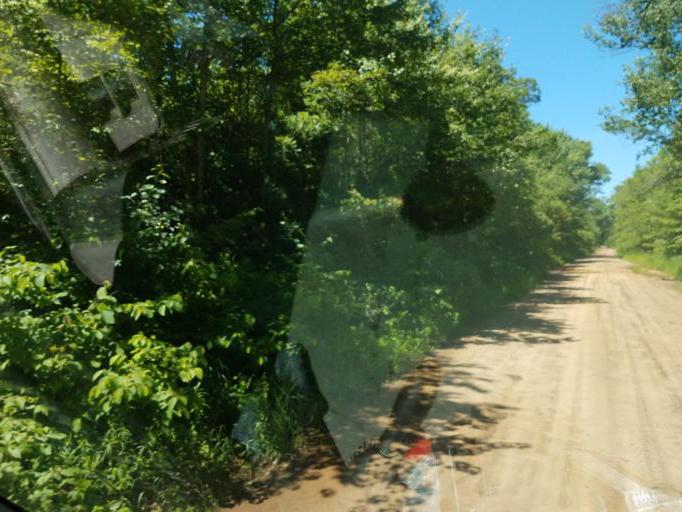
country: US
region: Wisconsin
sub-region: Adams County
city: Friendship
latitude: 44.0249
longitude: -89.9808
